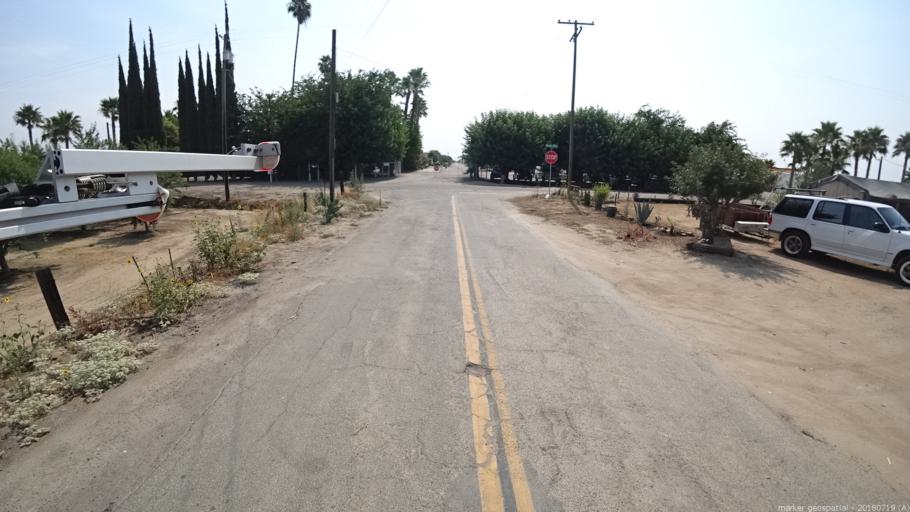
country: US
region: California
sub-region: Madera County
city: Fairmead
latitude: 37.0764
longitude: -120.1753
